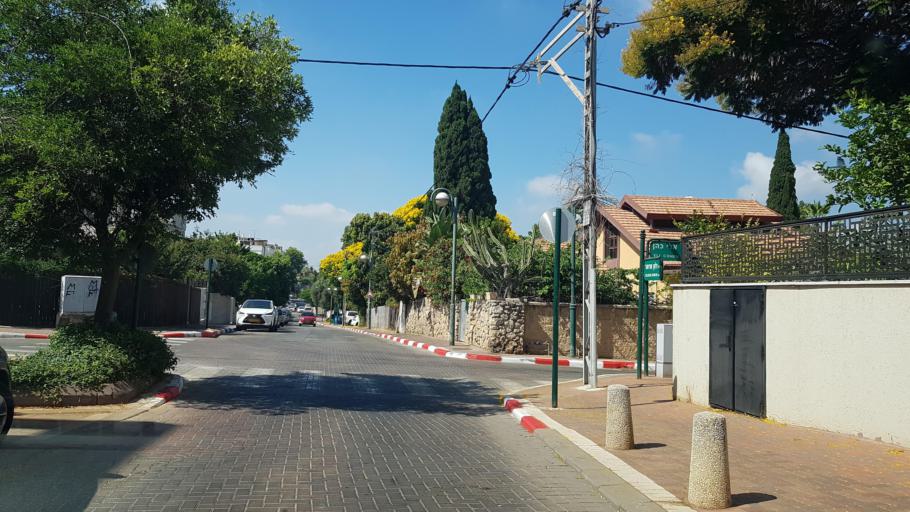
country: IL
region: Tel Aviv
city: Ramat HaSharon
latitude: 32.1485
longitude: 34.8387
